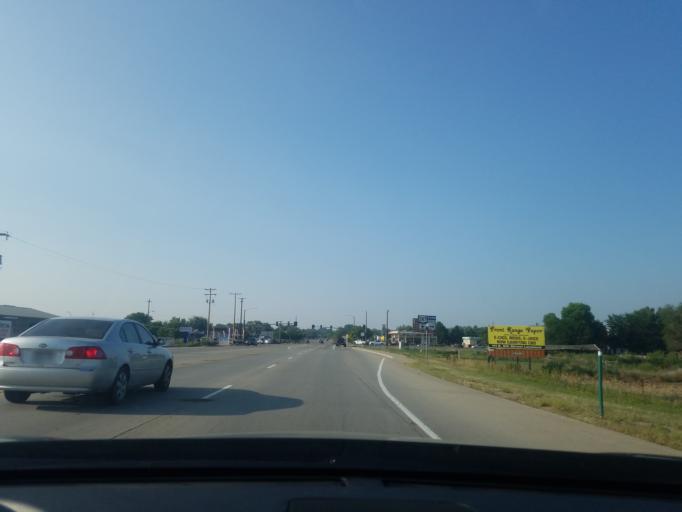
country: US
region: Colorado
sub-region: Larimer County
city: Loveland
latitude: 40.3767
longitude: -105.0732
